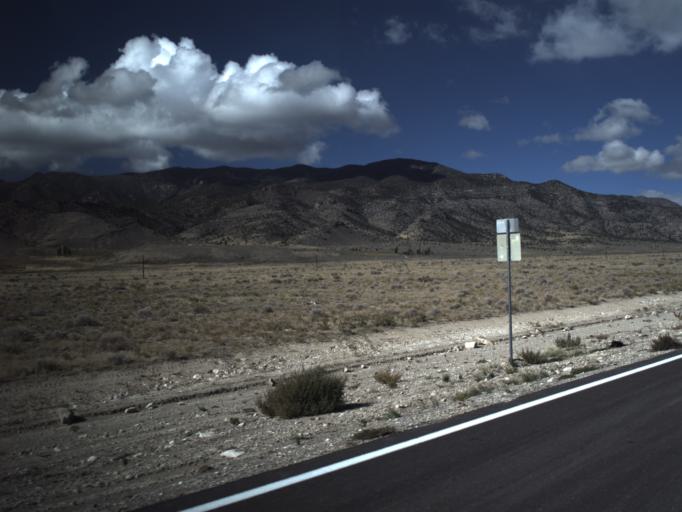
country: US
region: Utah
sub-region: Beaver County
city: Milford
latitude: 38.4920
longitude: -113.4730
